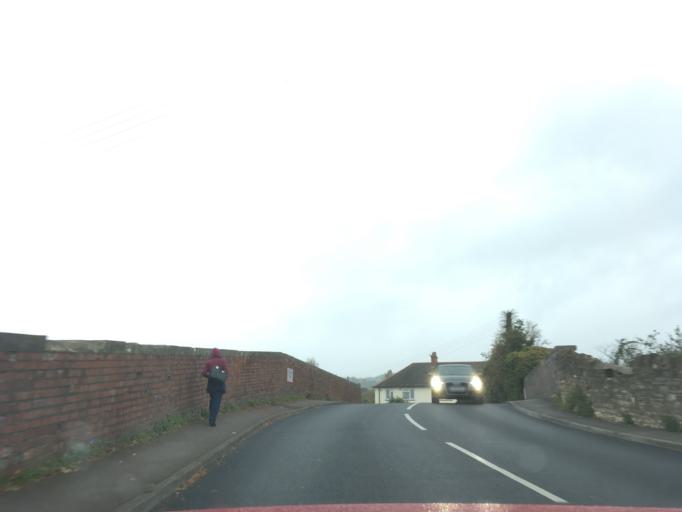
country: GB
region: England
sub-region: Gloucestershire
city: Stonehouse
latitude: 51.7451
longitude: -2.2434
